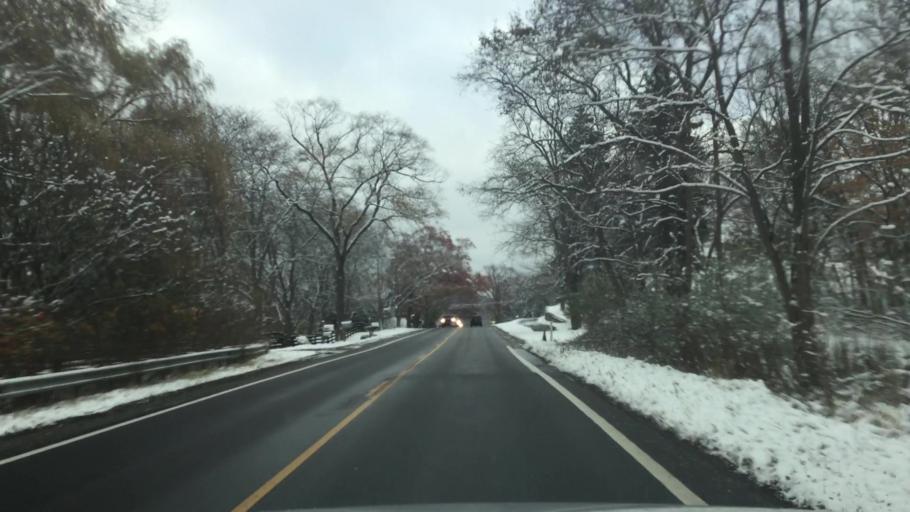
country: US
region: Michigan
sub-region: Oakland County
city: West Bloomfield Township
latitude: 42.5711
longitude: -83.3944
